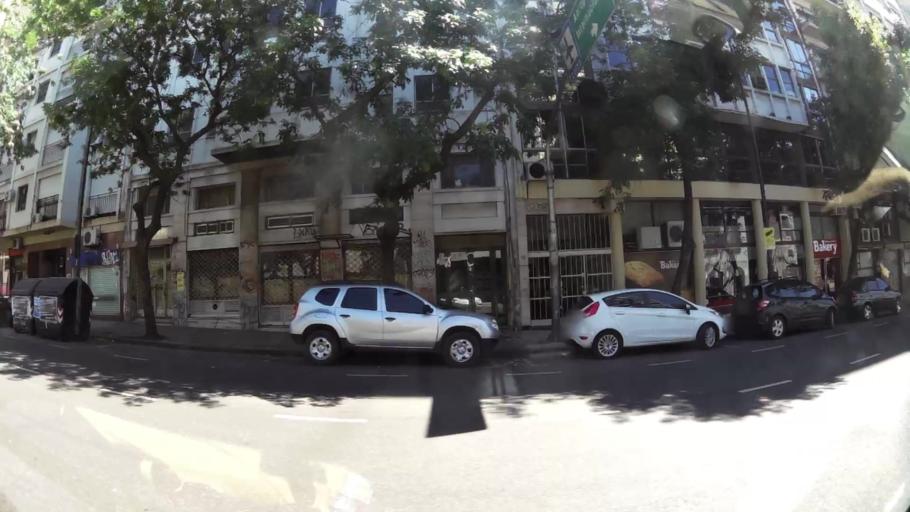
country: AR
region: Buenos Aires F.D.
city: Buenos Aires
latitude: -34.6121
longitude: -58.3701
